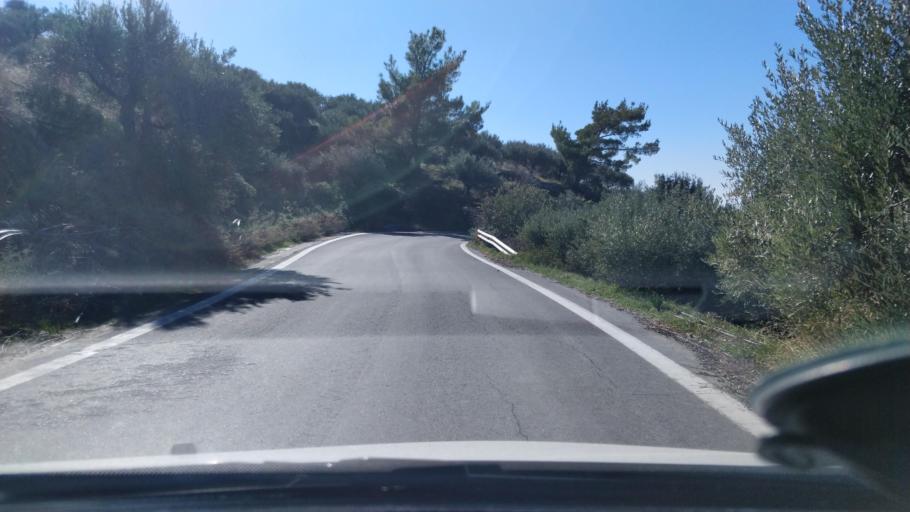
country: GR
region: Crete
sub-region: Nomos Irakleiou
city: Kastelli
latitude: 35.0148
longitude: 25.4476
